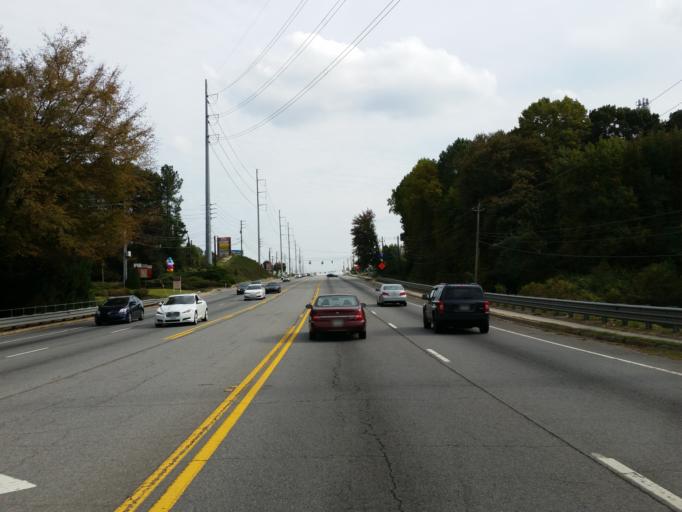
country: US
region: Georgia
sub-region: Cobb County
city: Vinings
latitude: 33.8945
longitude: -84.4797
